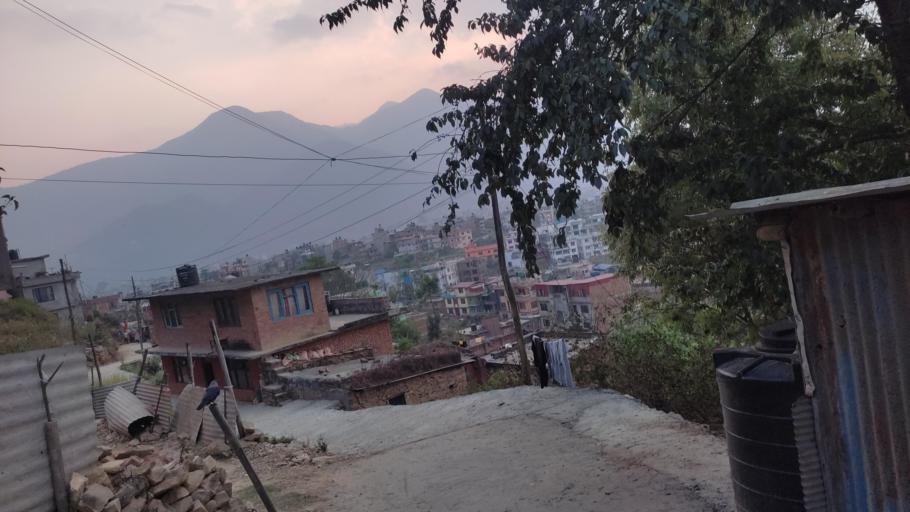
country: NP
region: Central Region
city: Kirtipur
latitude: 27.6695
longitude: 85.2886
